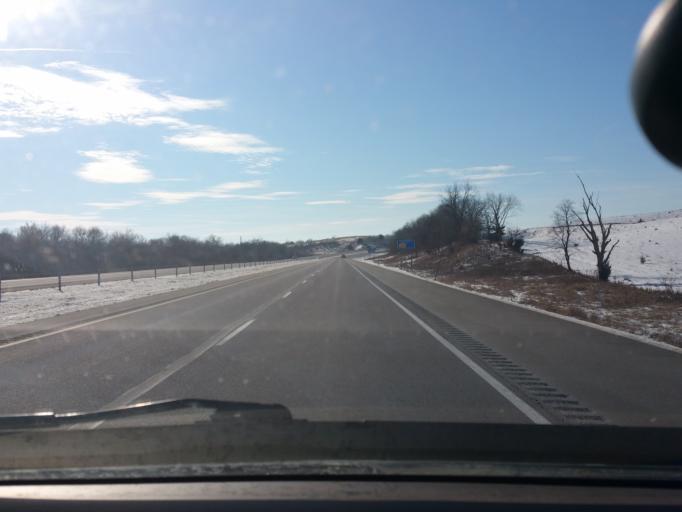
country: US
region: Iowa
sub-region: Clarke County
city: Osceola
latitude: 41.0580
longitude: -93.7818
